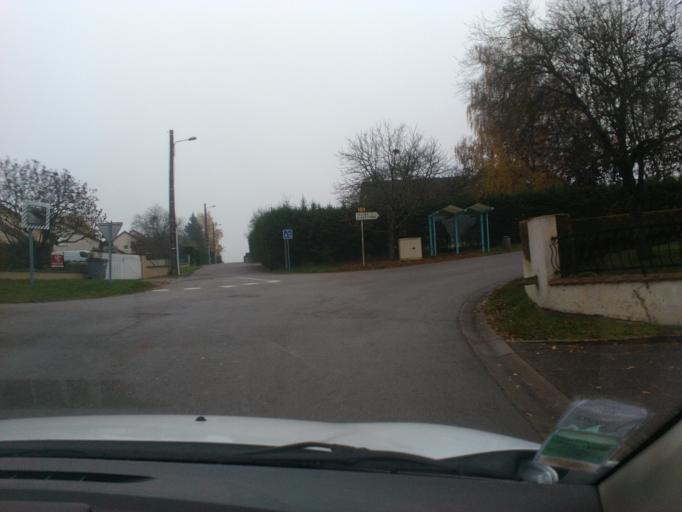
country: FR
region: Lorraine
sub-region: Departement des Vosges
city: Neufchateau
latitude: 48.3585
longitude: 5.7363
